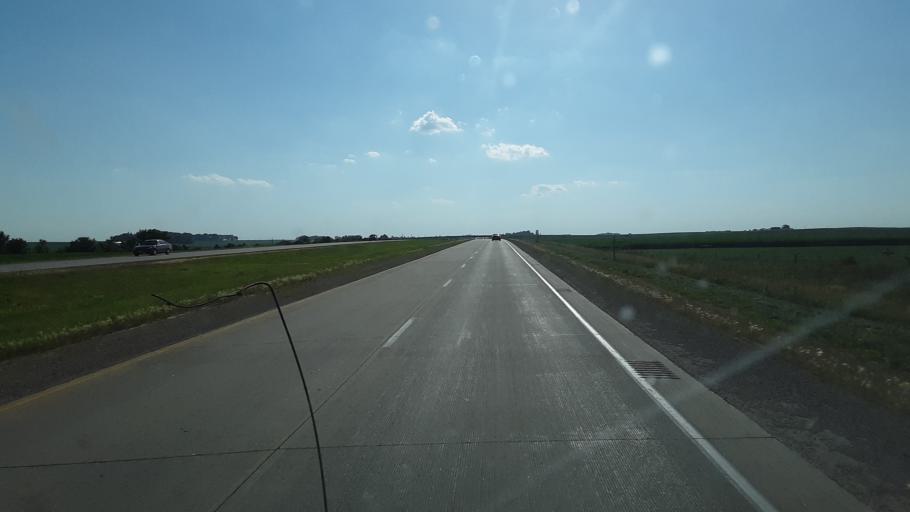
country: US
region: Iowa
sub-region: Grundy County
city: Dike
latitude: 42.4638
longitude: -92.6977
